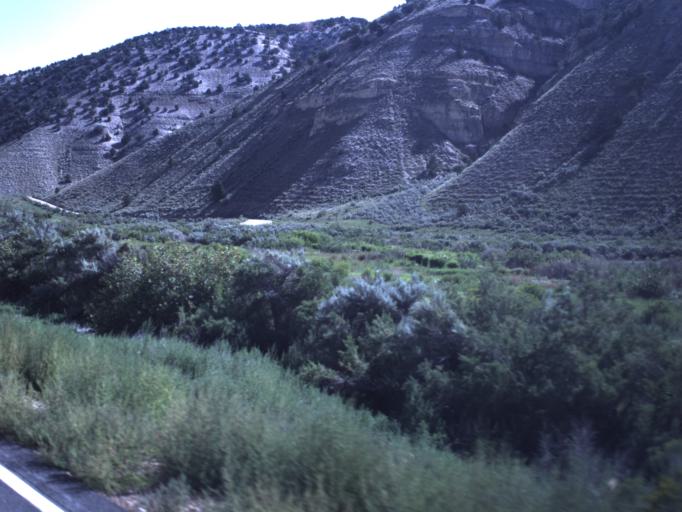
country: US
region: Utah
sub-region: Duchesne County
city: Duchesne
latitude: 40.0530
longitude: -110.5234
